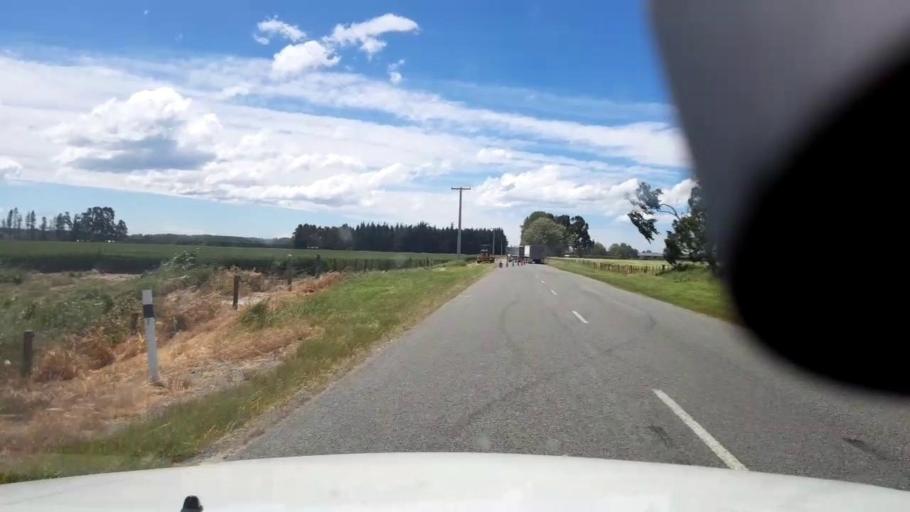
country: NZ
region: Canterbury
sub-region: Timaru District
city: Pleasant Point
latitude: -44.2799
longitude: 171.2465
